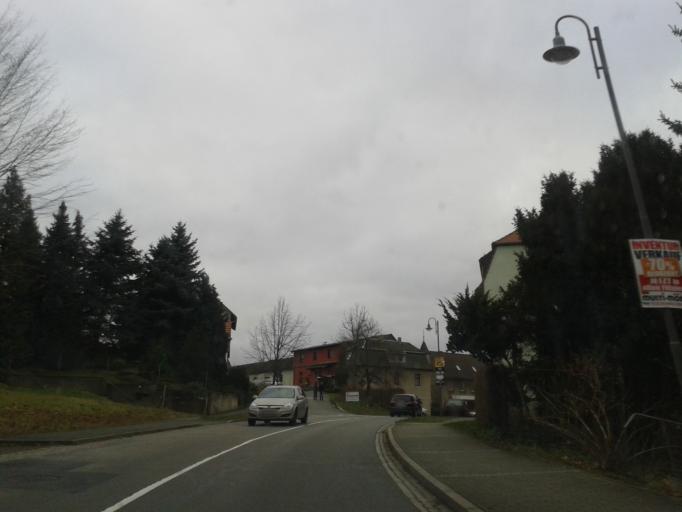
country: DE
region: Saxony
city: Weissenberg
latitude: 51.1946
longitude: 14.6551
